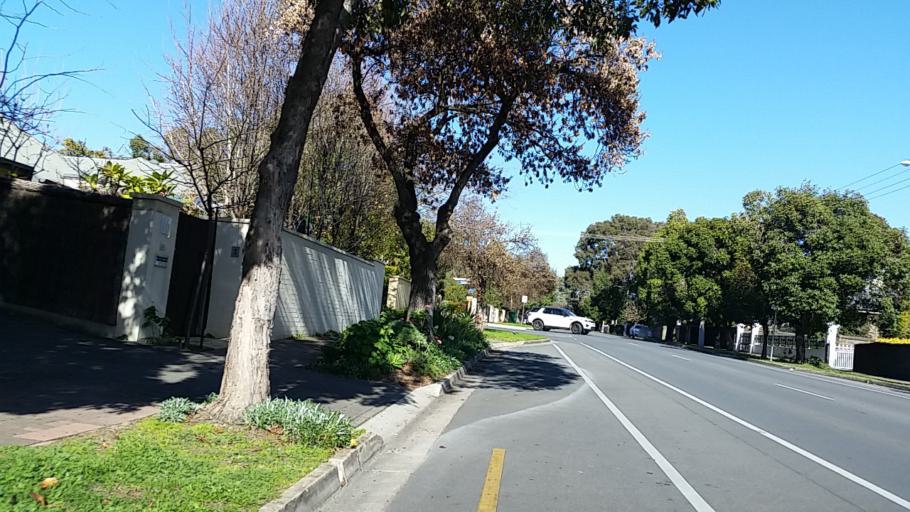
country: AU
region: South Australia
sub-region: Burnside
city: Leabrook
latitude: -34.9298
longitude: 138.6514
